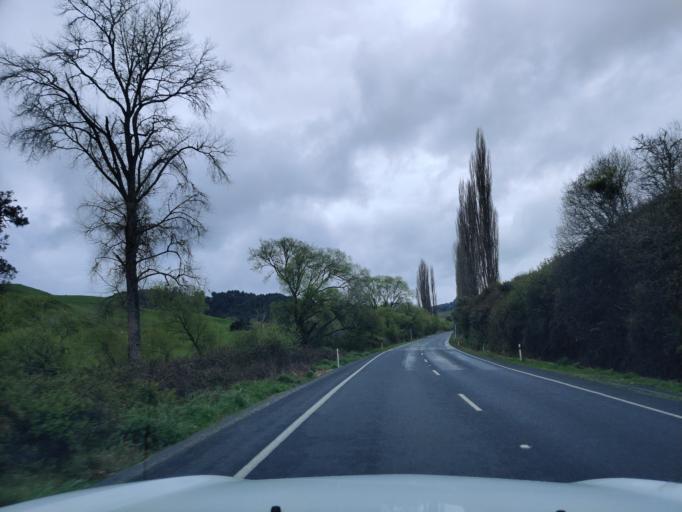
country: NZ
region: Waikato
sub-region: Otorohanga District
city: Otorohanga
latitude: -38.5633
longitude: 175.1982
